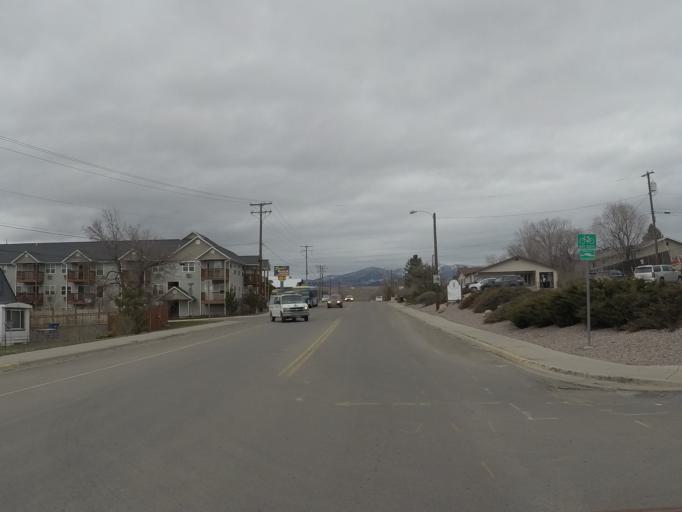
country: US
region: Montana
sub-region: Missoula County
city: Missoula
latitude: 46.8810
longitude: -114.0185
